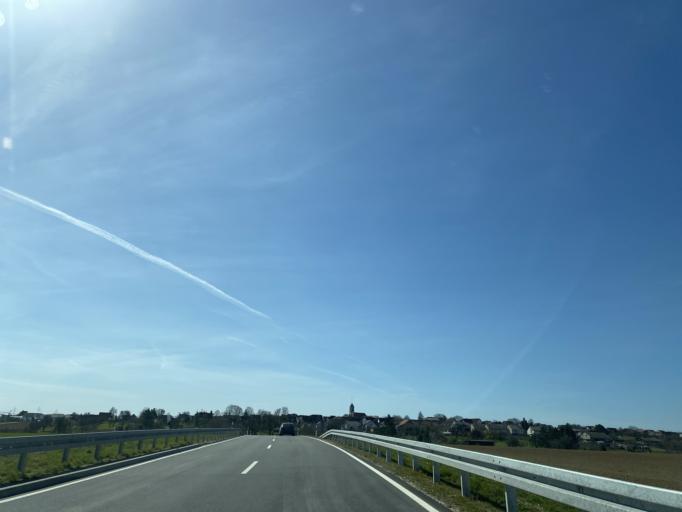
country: DE
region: Baden-Wuerttemberg
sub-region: Regierungsbezirk Stuttgart
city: Eberdingen
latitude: 48.8601
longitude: 8.9852
